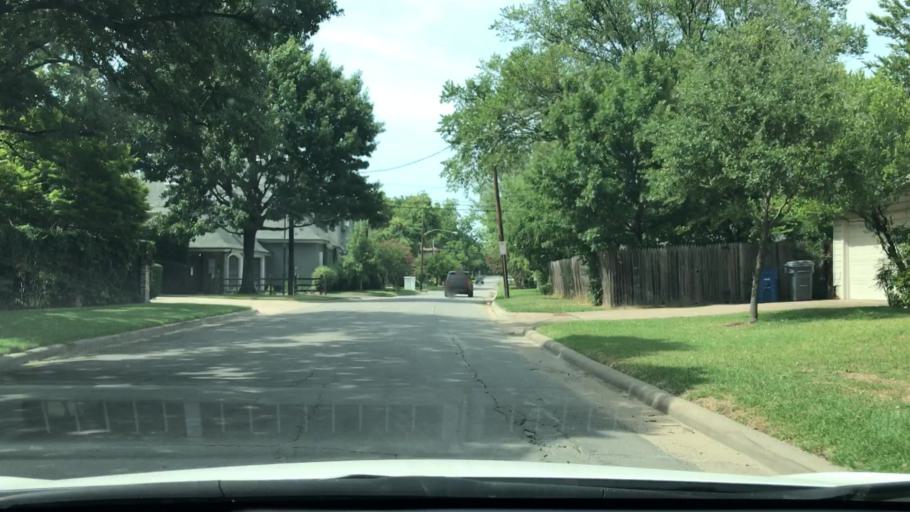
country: US
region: Texas
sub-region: Dallas County
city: University Park
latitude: 32.8813
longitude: -96.7900
